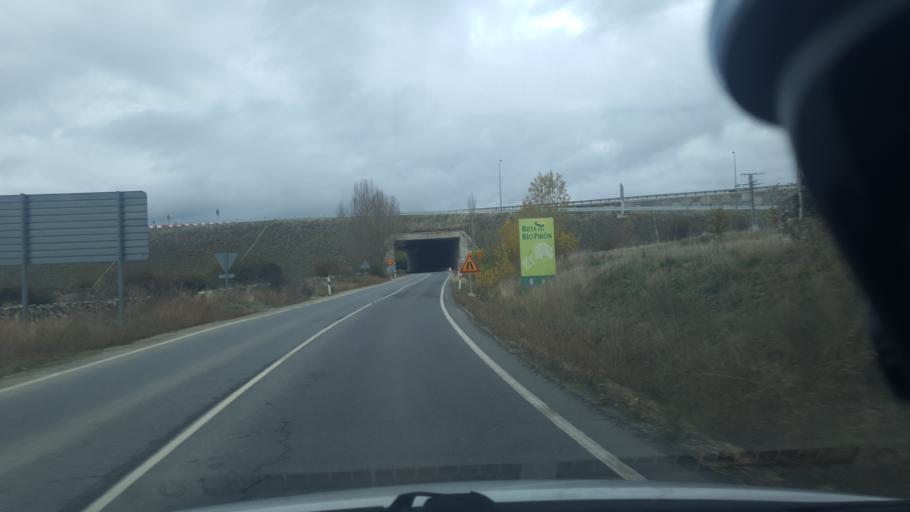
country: ES
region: Castille and Leon
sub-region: Provincia de Segovia
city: La Lastrilla
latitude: 40.9730
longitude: -4.0886
